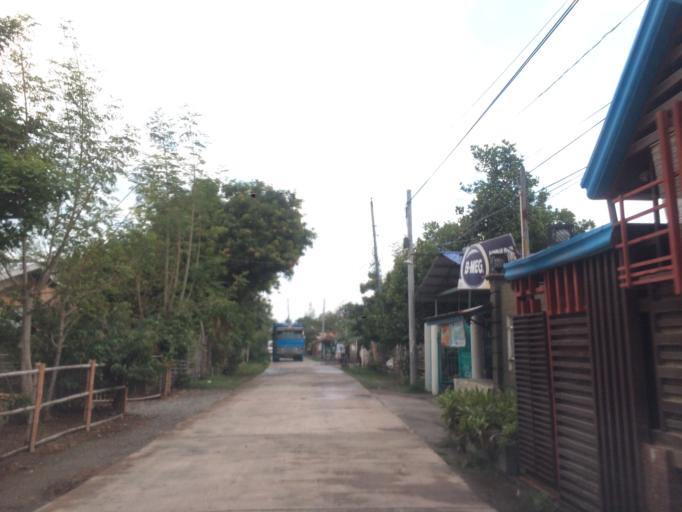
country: PH
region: Ilocos
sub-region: Province of Pangasinan
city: Dumpay
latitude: 15.8782
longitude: 120.3865
